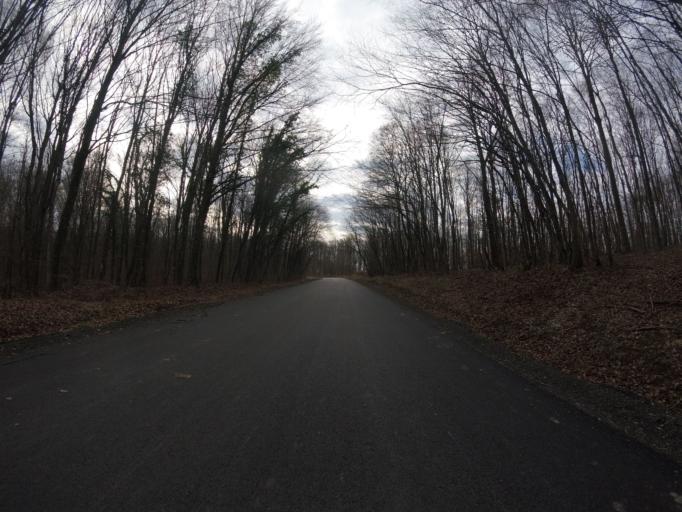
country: HR
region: Sisacko-Moslavacka
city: Glina
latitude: 45.5008
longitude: 16.0428
